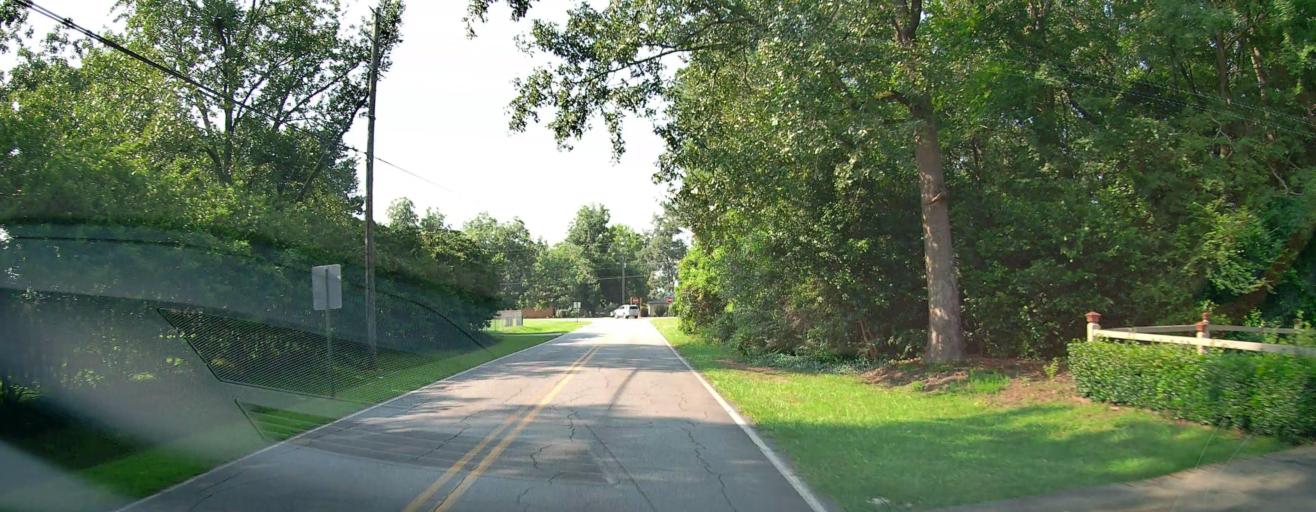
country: US
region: Georgia
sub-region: Houston County
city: Centerville
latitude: 32.7314
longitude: -83.6892
